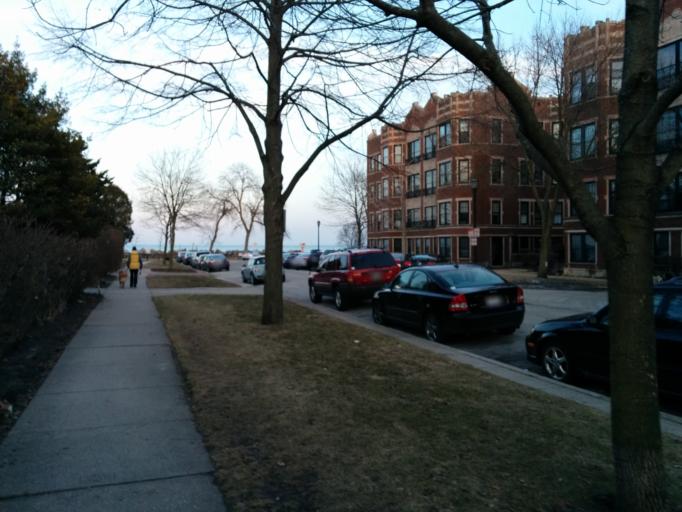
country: US
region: Illinois
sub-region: Cook County
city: Evanston
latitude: 42.0294
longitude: -87.6701
